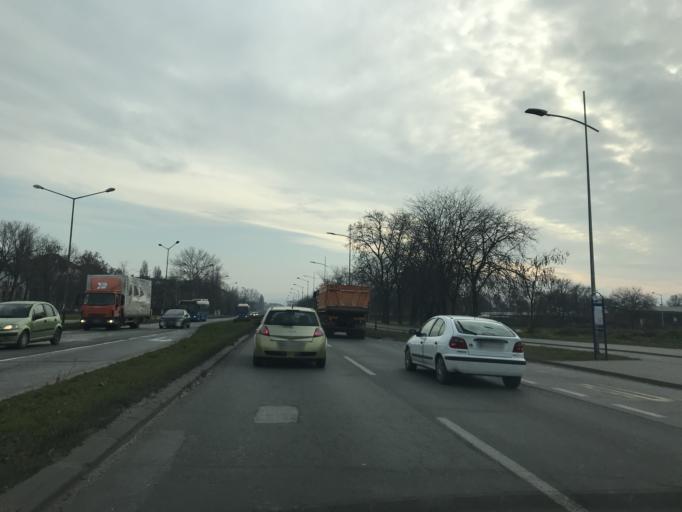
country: RS
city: Veternik
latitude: 45.2489
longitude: 19.7922
